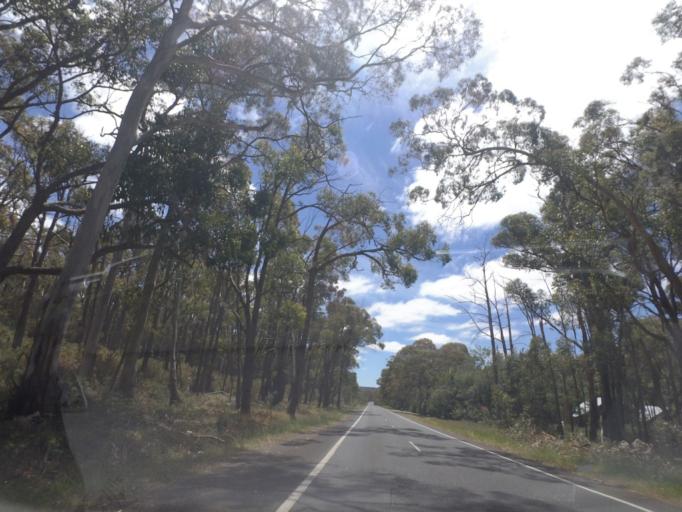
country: AU
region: Victoria
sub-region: Mount Alexander
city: Castlemaine
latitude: -37.3064
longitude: 144.1644
